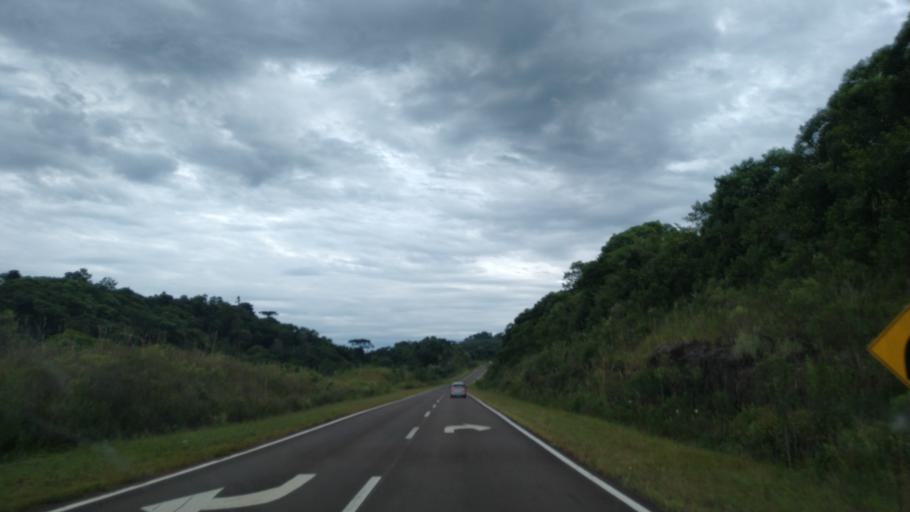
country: AR
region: Misiones
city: Bernardo de Irigoyen
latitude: -26.3269
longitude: -53.7584
